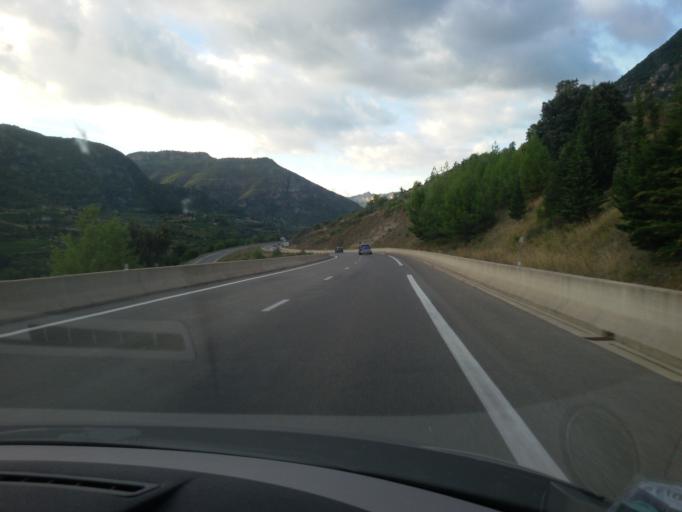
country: FR
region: Languedoc-Roussillon
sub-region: Departement de l'Herault
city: Lodeve
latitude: 43.7818
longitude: 3.3296
